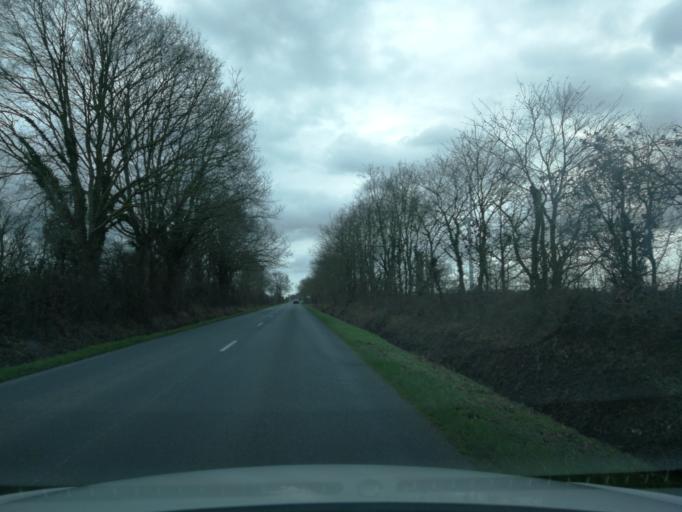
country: FR
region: Pays de la Loire
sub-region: Departement de la Loire-Atlantique
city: La Planche
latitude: 47.0061
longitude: -1.4734
